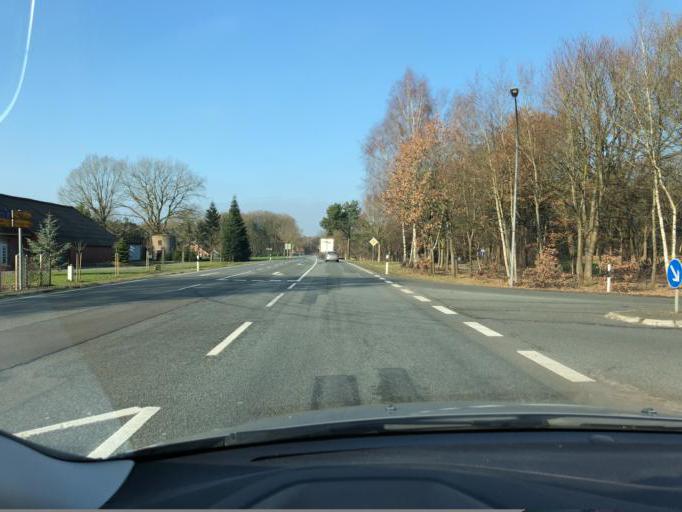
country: DE
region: Lower Saxony
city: Schwerinsdorf
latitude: 53.3057
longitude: 7.7720
